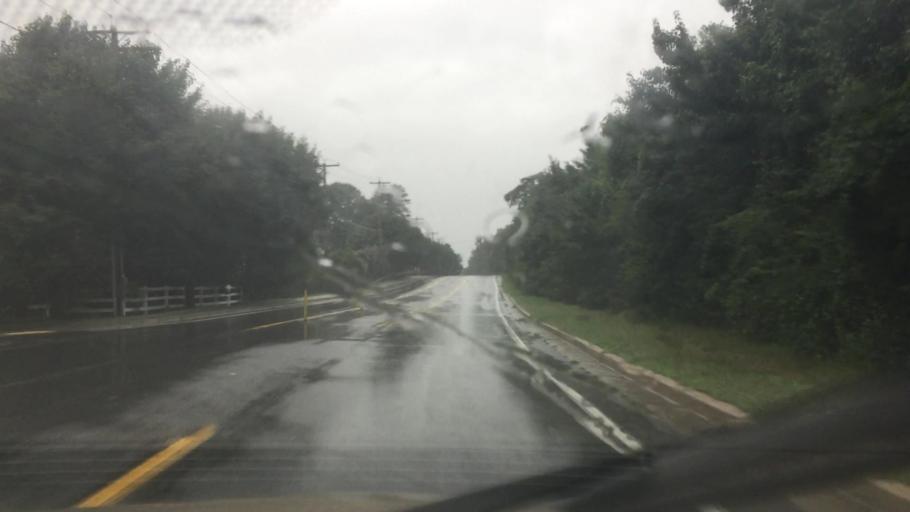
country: US
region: Maryland
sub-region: Anne Arundel County
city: Severn
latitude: 39.1354
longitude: -76.7145
